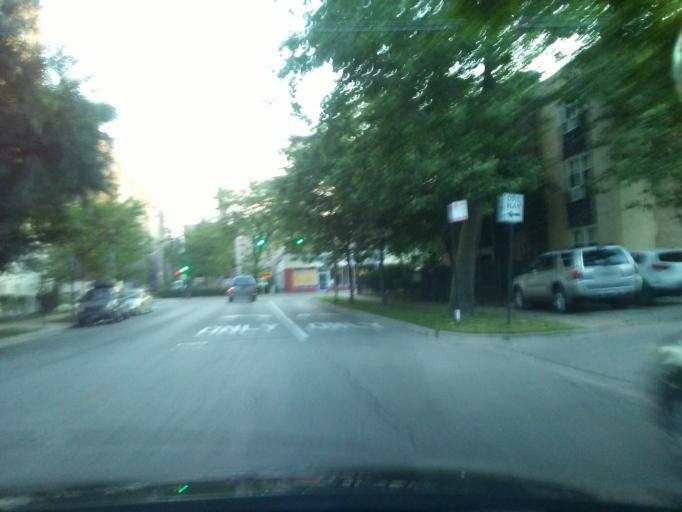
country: US
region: Illinois
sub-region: Cook County
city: Evanston
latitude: 42.0048
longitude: -87.6706
